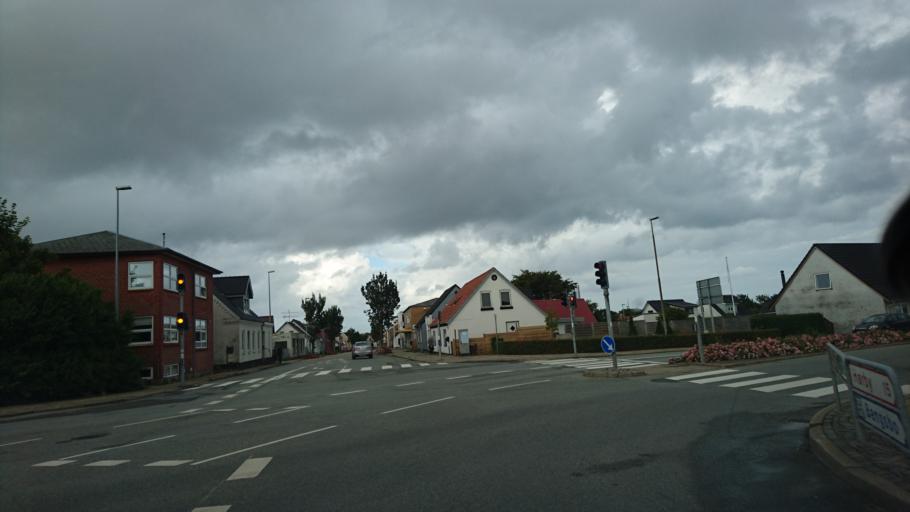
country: DK
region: North Denmark
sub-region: Frederikshavn Kommune
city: Frederikshavn
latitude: 57.4273
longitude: 10.5203
